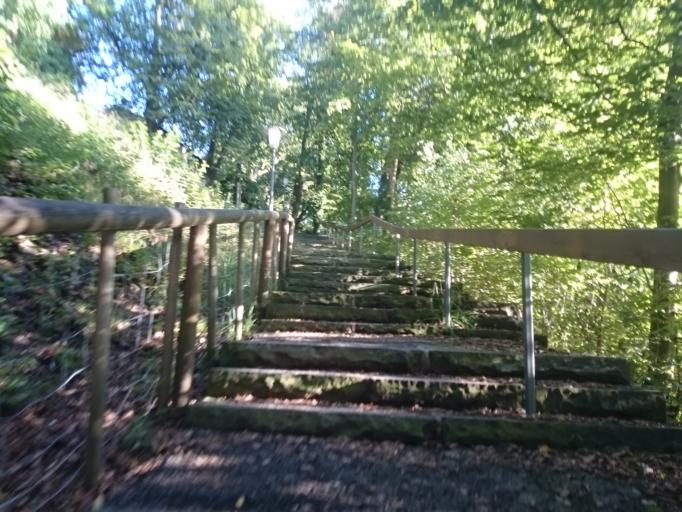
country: DE
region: Bavaria
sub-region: Swabia
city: Kempten (Allgaeu)
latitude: 47.7236
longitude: 10.3197
